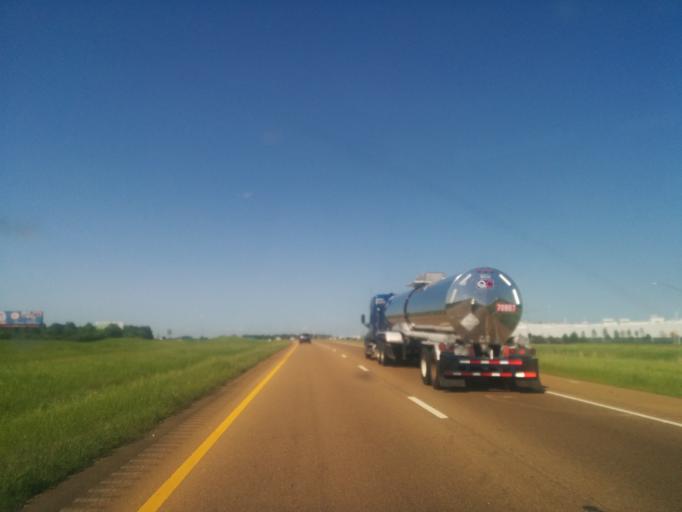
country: US
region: Mississippi
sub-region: Madison County
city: Canton
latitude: 32.5674
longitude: -90.0769
